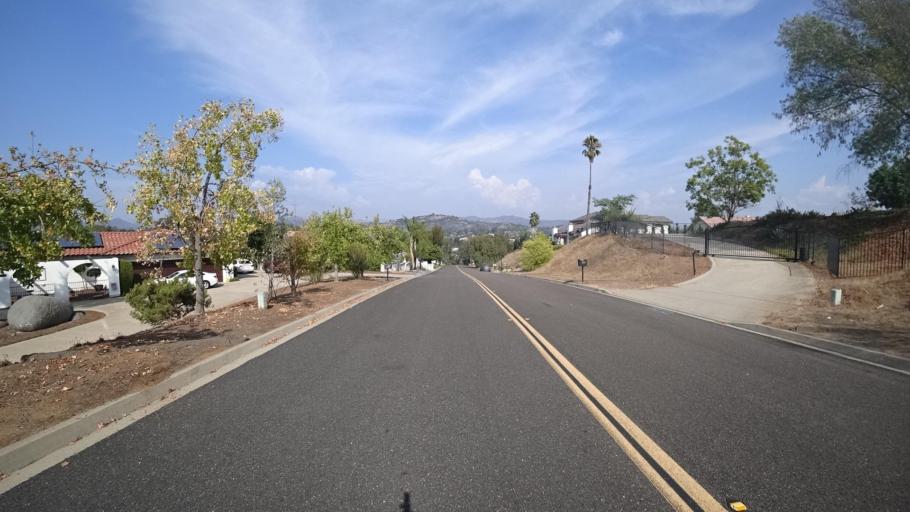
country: US
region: California
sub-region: San Diego County
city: Escondido
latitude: 33.1076
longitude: -117.0574
